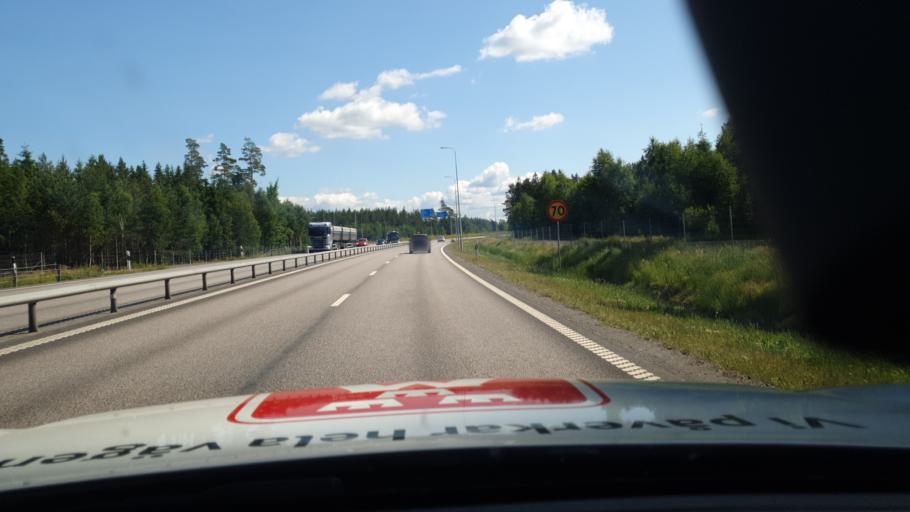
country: SE
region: Vaestra Goetaland
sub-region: Lidkopings Kommun
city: Lidkoping
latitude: 58.4814
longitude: 13.1991
